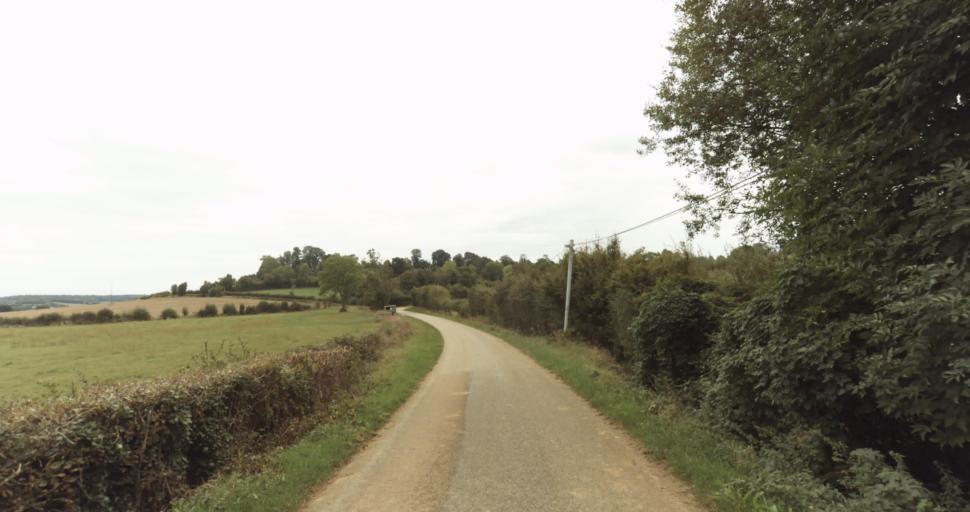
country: FR
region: Lower Normandy
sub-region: Departement de l'Orne
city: Gace
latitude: 48.7502
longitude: 0.3372
